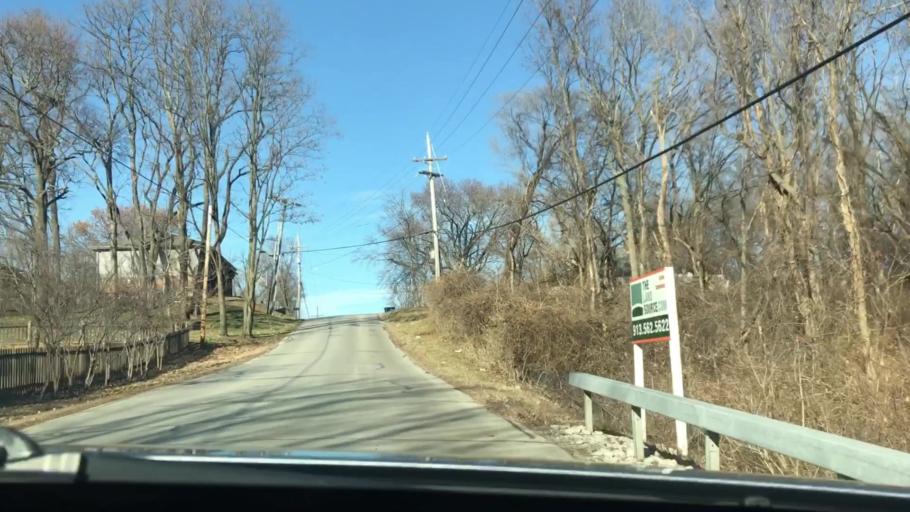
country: US
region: Missouri
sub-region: Platte County
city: Parkville
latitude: 39.2022
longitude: -94.6871
